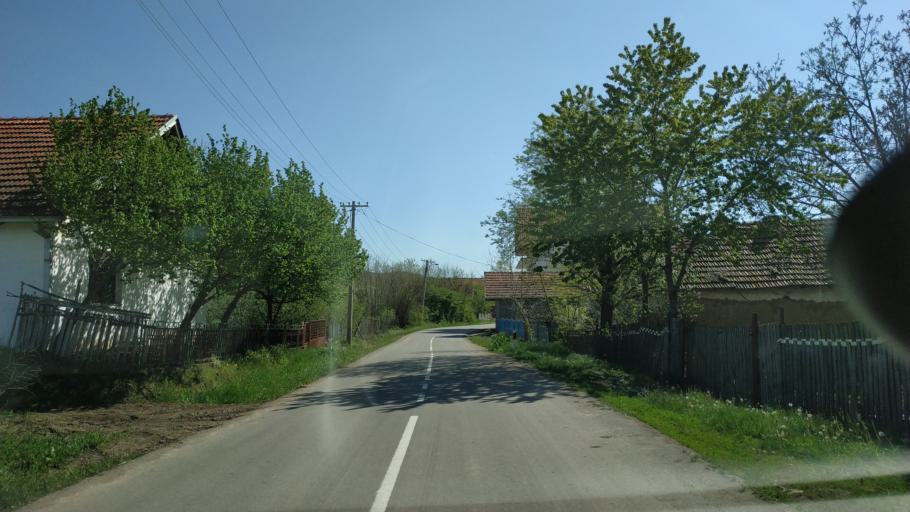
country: RS
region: Central Serbia
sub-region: Nisavski Okrug
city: Nis
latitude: 43.4669
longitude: 21.8627
